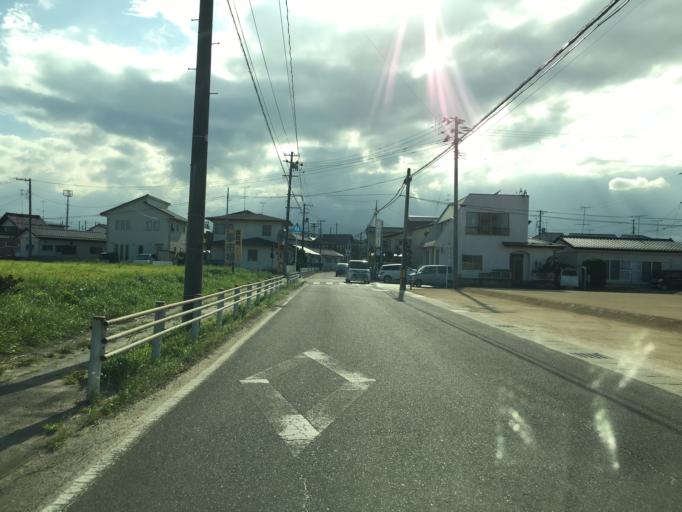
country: JP
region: Fukushima
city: Hobaramachi
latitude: 37.8239
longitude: 140.5628
